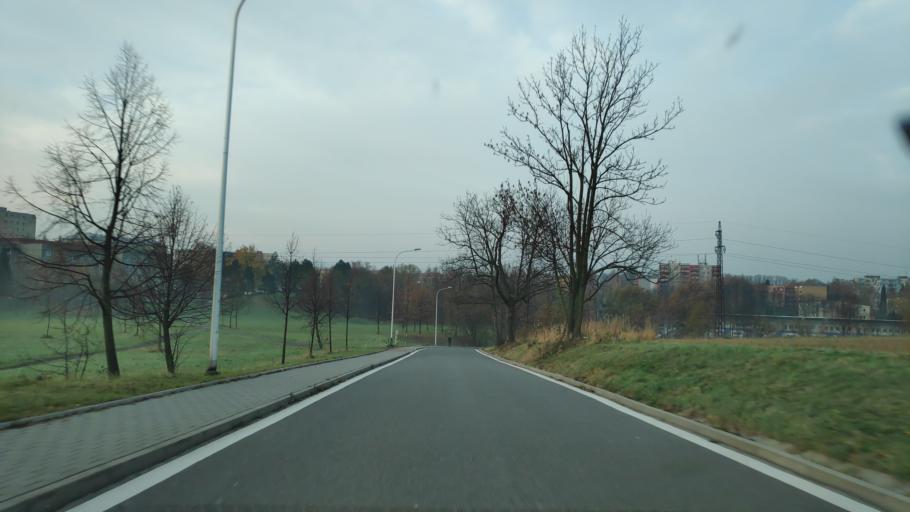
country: CZ
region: Moravskoslezsky
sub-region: Okres Frydek-Mistek
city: Frydek-Mistek
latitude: 49.6958
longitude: 18.3474
